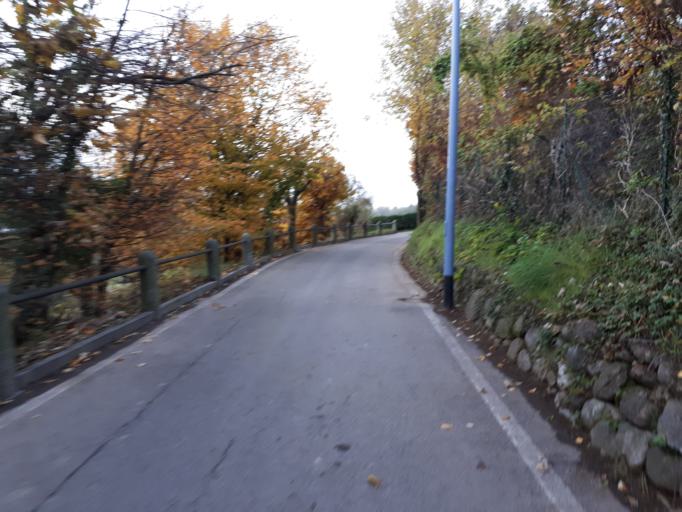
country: IT
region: Lombardy
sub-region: Provincia di Lecco
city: Cernusco Lombardone
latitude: 45.6940
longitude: 9.3950
